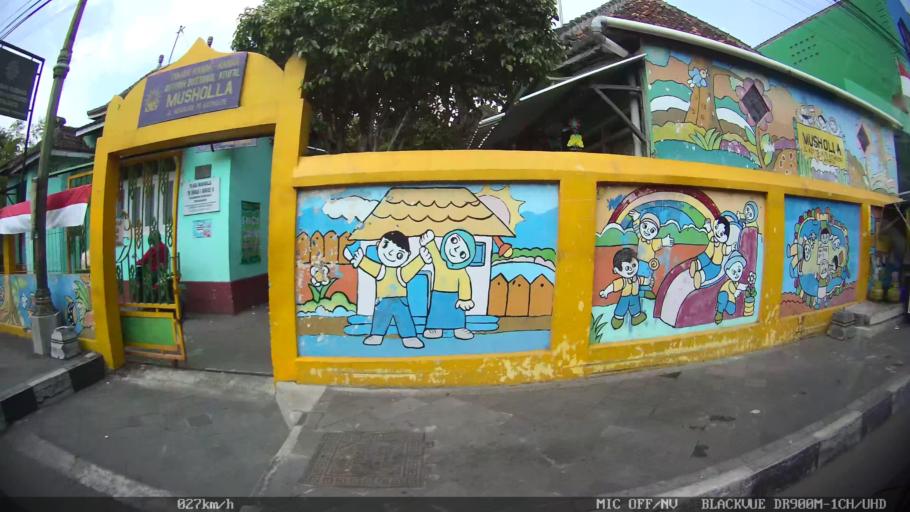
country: ID
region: Daerah Istimewa Yogyakarta
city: Yogyakarta
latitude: -7.8268
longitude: 110.4005
